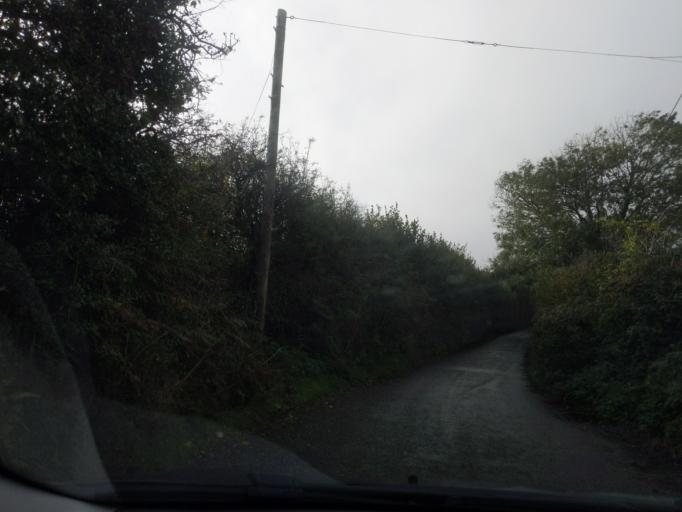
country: GB
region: England
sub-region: Cornwall
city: Looe
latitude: 50.3660
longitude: -4.3974
